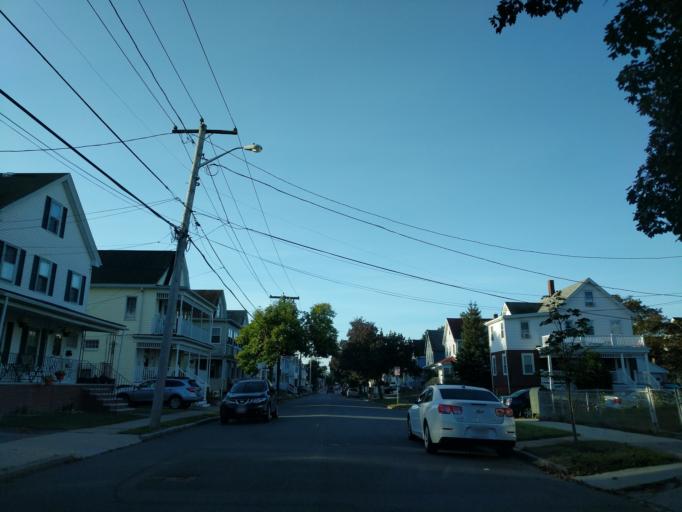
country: US
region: Massachusetts
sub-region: Middlesex County
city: Medford
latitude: 42.4209
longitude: -71.0918
